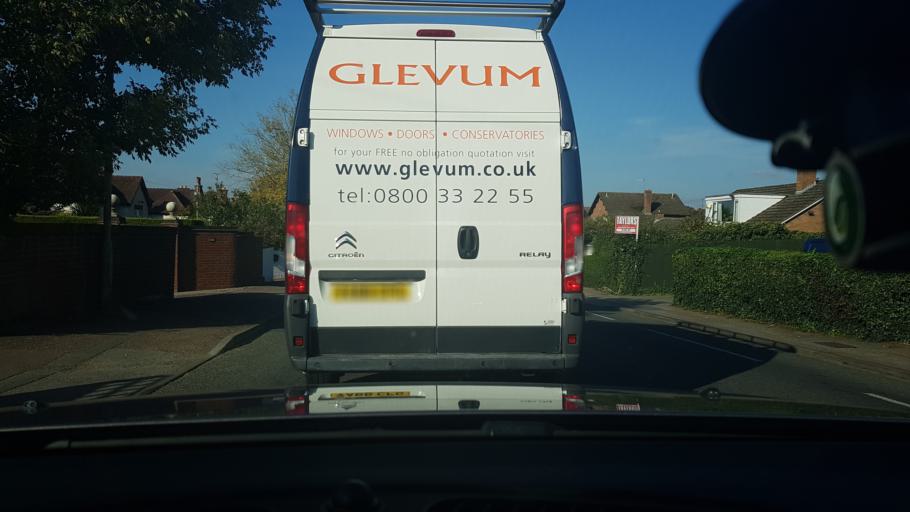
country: GB
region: England
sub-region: Gloucestershire
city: Gloucester
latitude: 51.8374
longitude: -2.2429
